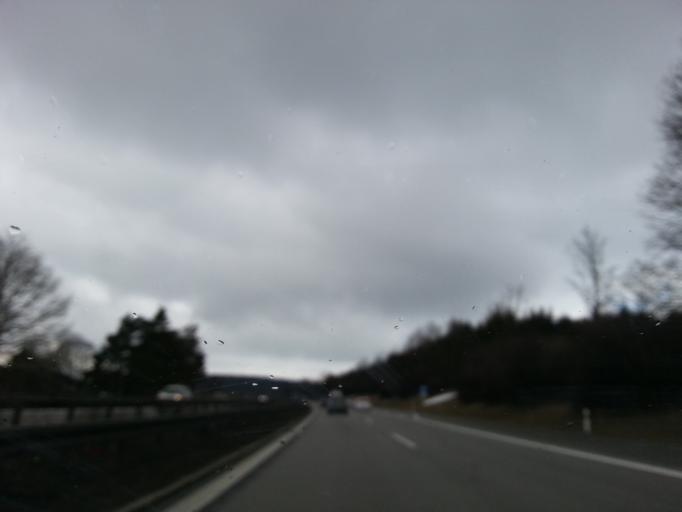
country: DE
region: Bavaria
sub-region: Upper Palatinate
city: Hohenfels
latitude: 49.1660
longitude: 11.8334
